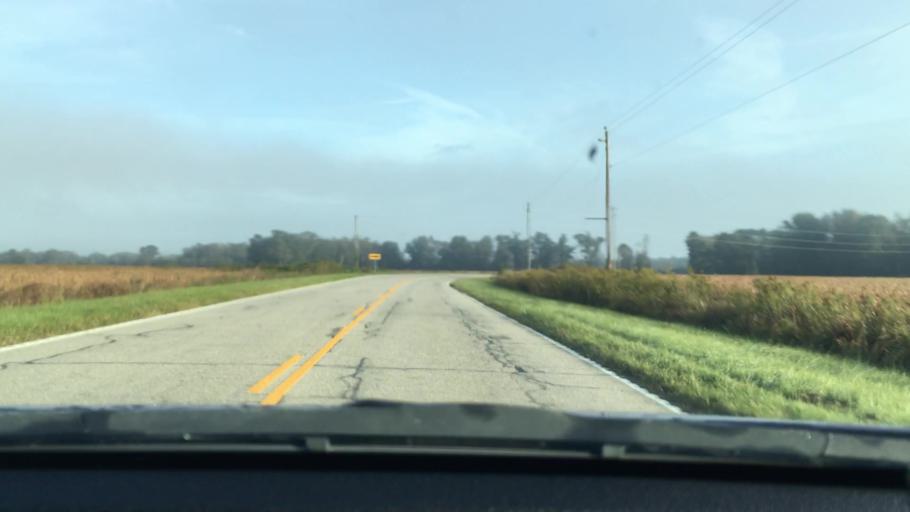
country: US
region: South Carolina
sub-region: Sumter County
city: East Sumter
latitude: 33.9860
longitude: -80.2967
